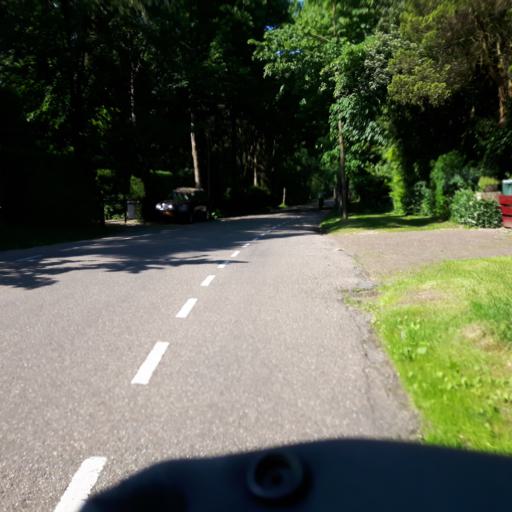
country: NL
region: Utrecht
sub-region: Gemeente Zeist
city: Zeist
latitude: 52.1307
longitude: 5.2380
